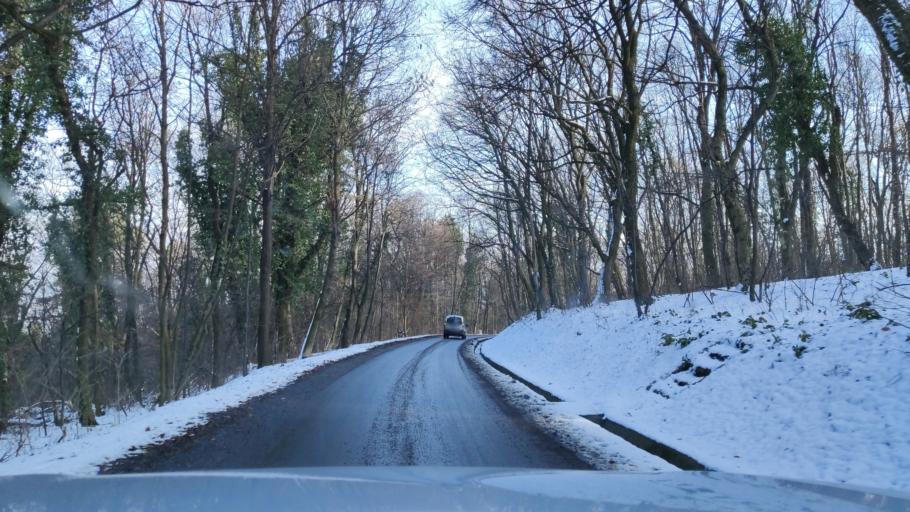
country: RS
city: Rusanj
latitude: 44.6982
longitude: 20.5183
